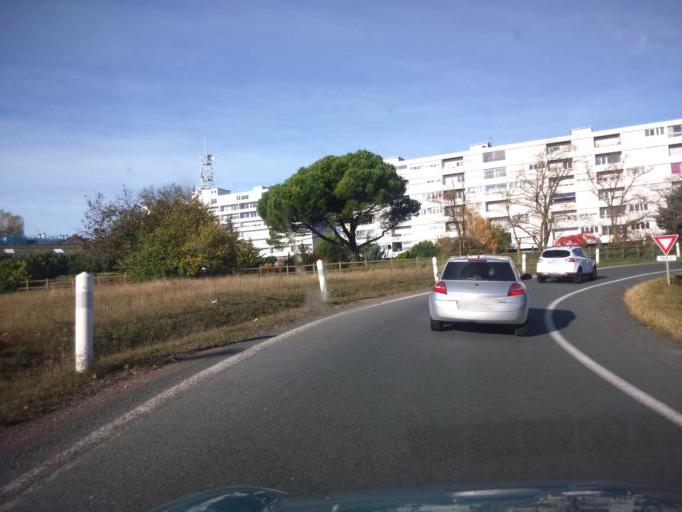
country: FR
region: Poitou-Charentes
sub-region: Departement de la Charente-Maritime
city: Puilboreau
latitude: 46.1718
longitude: -1.1222
